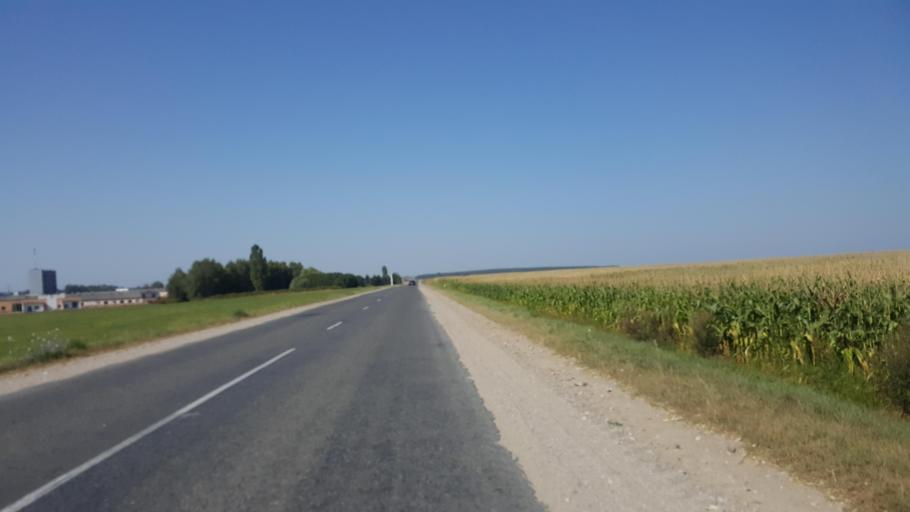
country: BY
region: Brest
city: Kamyanyets
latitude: 52.4175
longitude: 23.6952
